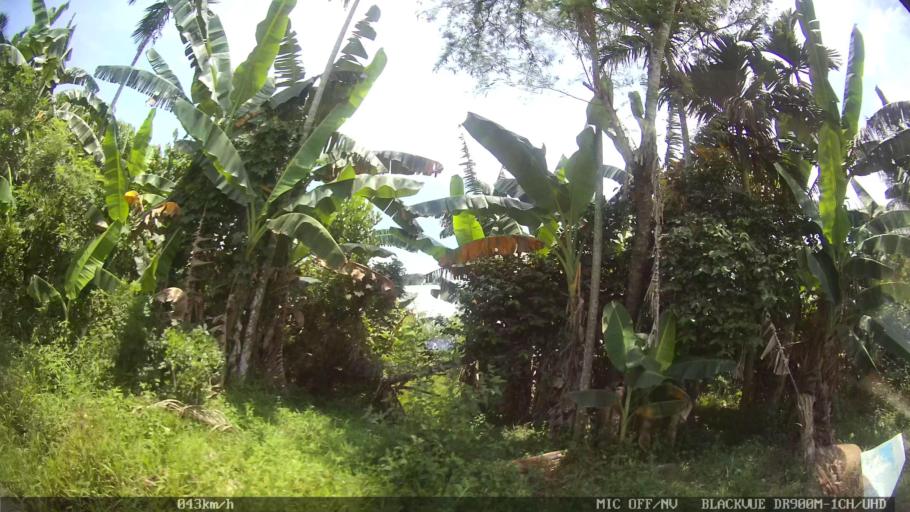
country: ID
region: North Sumatra
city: Binjai
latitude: 3.5929
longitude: 98.5368
